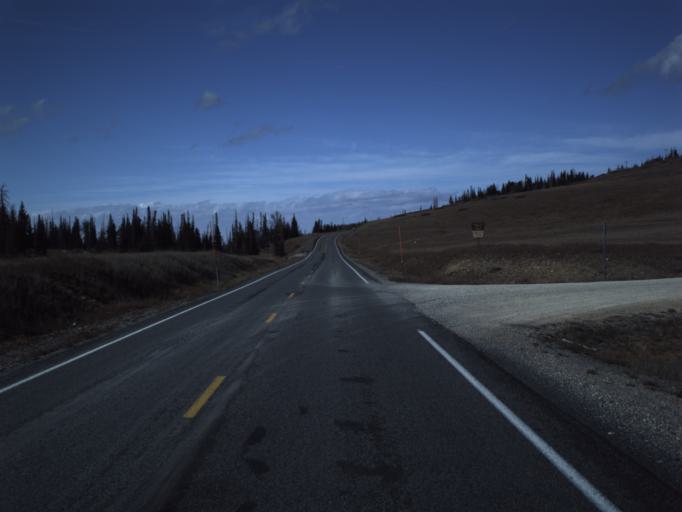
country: US
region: Utah
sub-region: Iron County
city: Parowan
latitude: 37.6686
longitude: -112.8392
